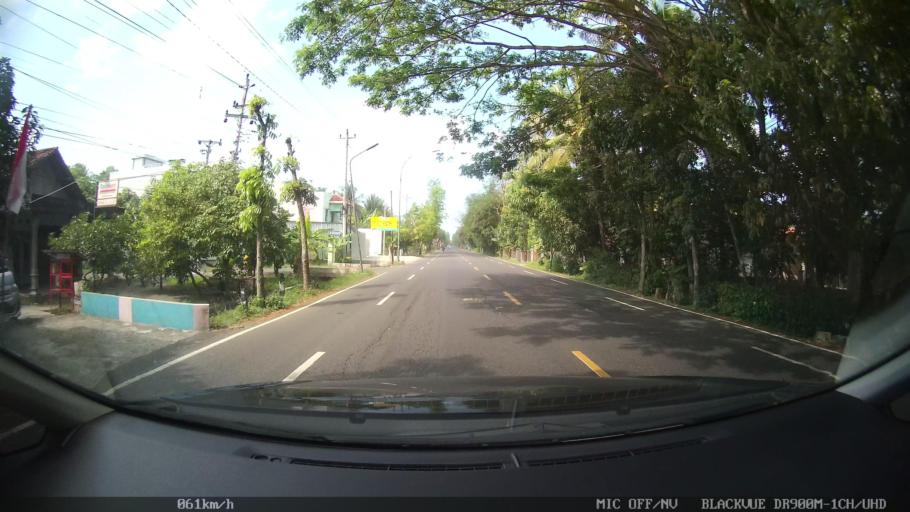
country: ID
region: Daerah Istimewa Yogyakarta
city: Srandakan
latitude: -7.8858
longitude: 110.1308
